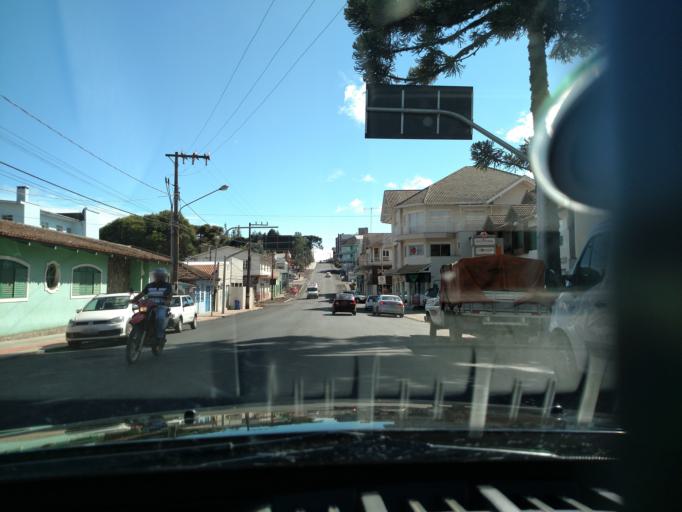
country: BR
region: Santa Catarina
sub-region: Sao Joaquim
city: Sao Joaquim
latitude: -28.2913
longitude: -49.9365
